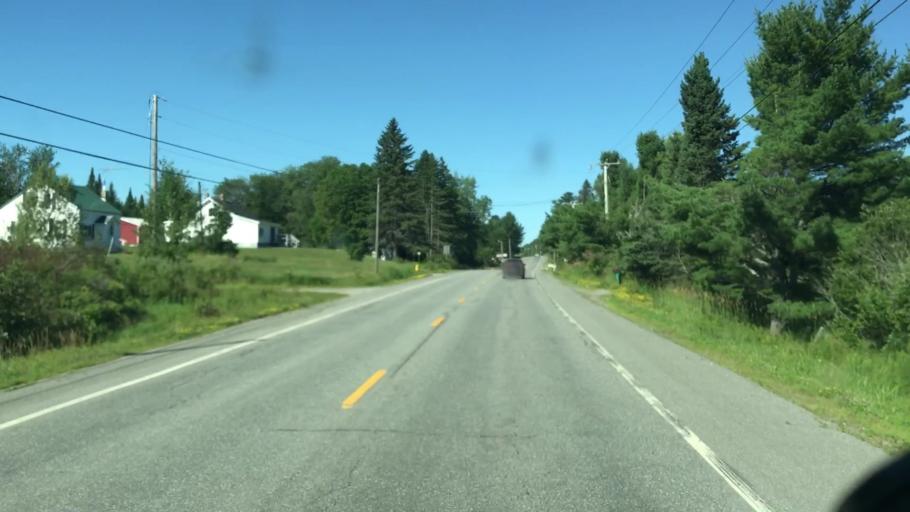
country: US
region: Maine
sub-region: Penobscot County
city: Lincoln
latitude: 45.3478
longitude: -68.5487
